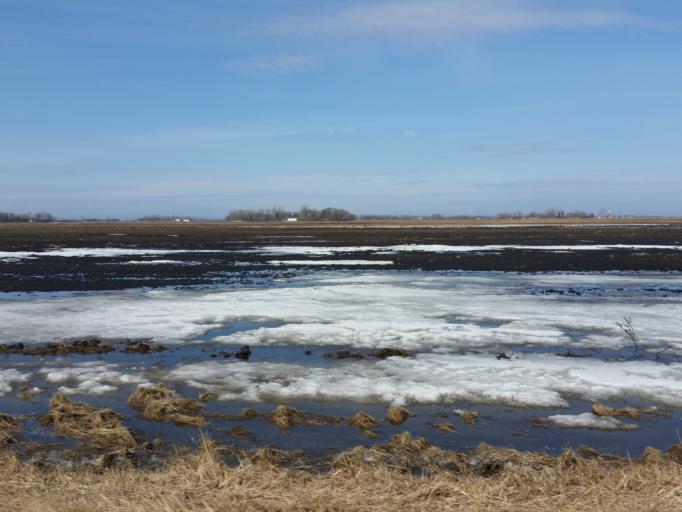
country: US
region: North Dakota
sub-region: Walsh County
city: Grafton
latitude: 48.4413
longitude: -97.4081
